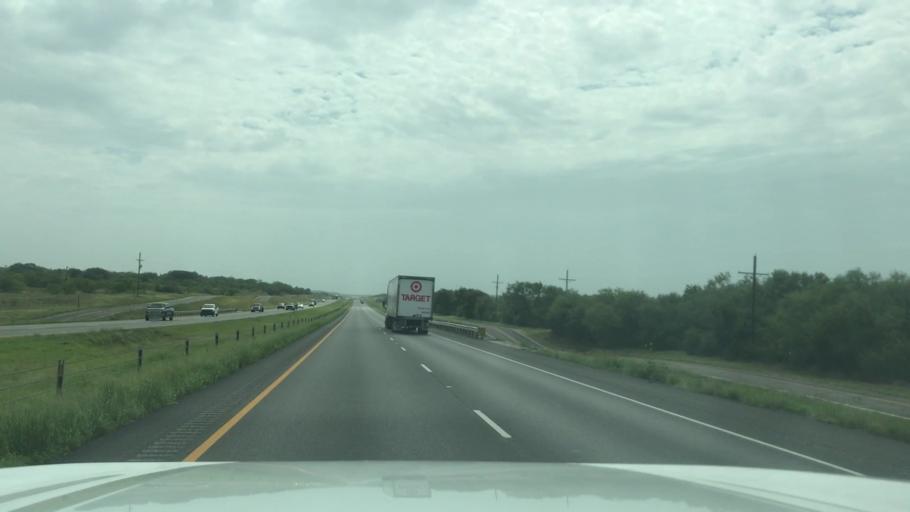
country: US
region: Texas
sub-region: Callahan County
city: Baird
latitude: 32.3843
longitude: -99.2881
